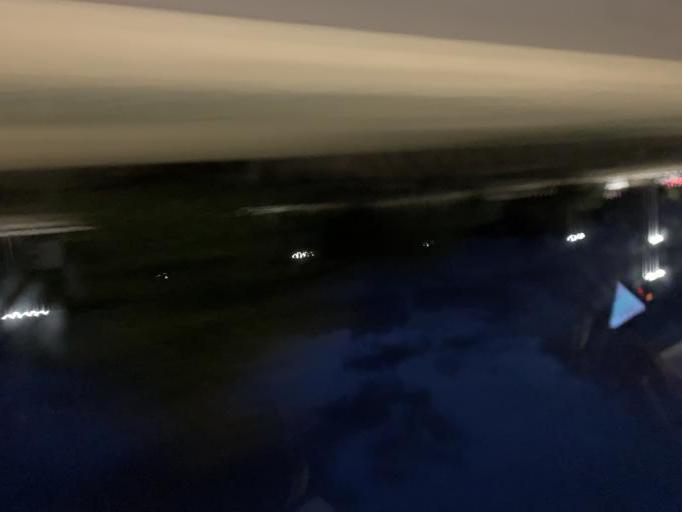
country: ES
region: Extremadura
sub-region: Provincia de Badajoz
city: Badajoz
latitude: 38.8887
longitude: -6.9188
